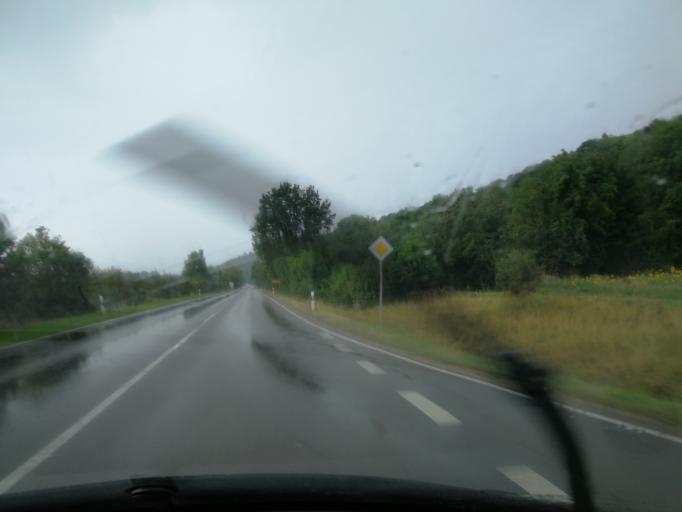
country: DE
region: Bavaria
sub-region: Upper Palatinate
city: Donaustauf
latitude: 49.0288
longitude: 12.2316
